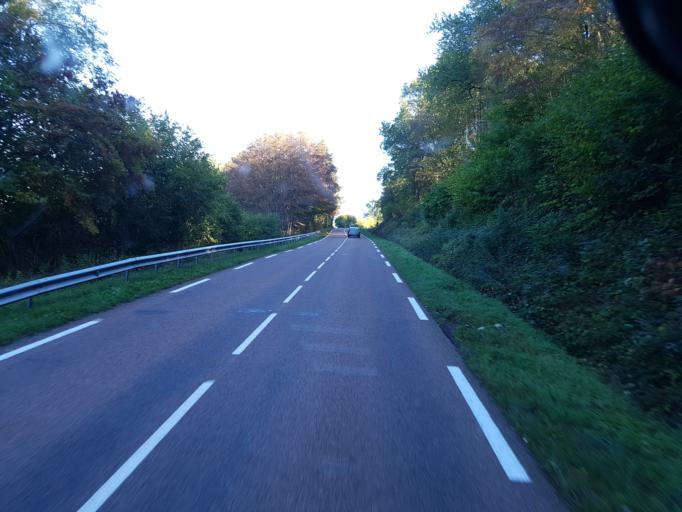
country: FR
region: Bourgogne
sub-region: Departement de Saone-et-Loire
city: Autun
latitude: 47.0472
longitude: 4.2733
